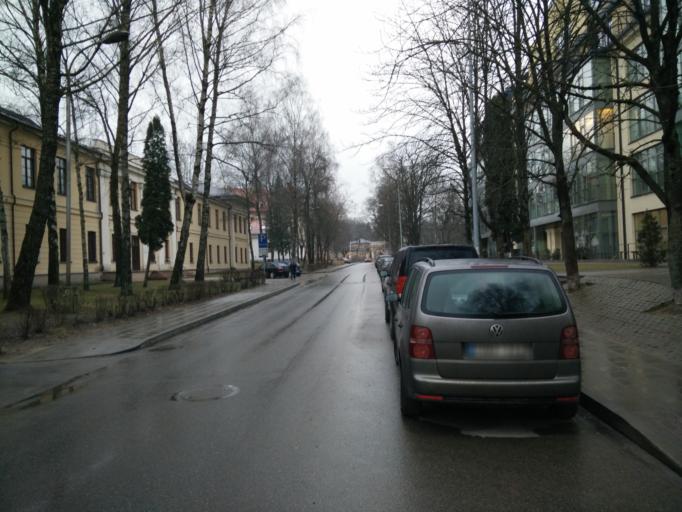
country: LT
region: Vilnius County
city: Rasos
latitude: 54.7002
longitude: 25.3140
